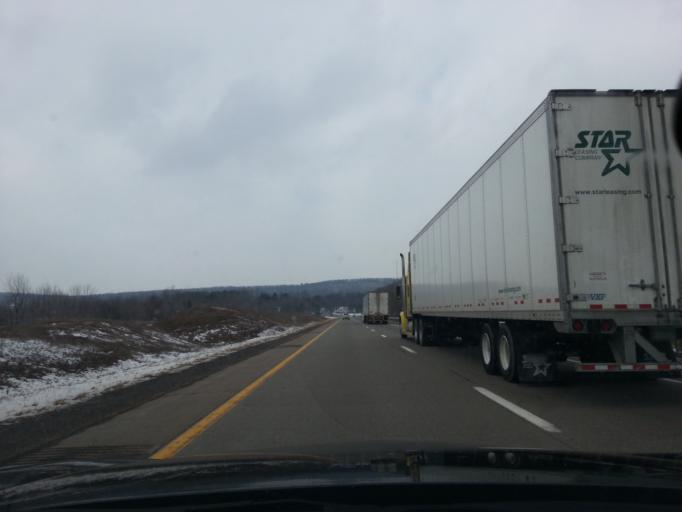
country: US
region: Pennsylvania
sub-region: Luzerne County
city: Conyngham
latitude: 41.0355
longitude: -76.0129
